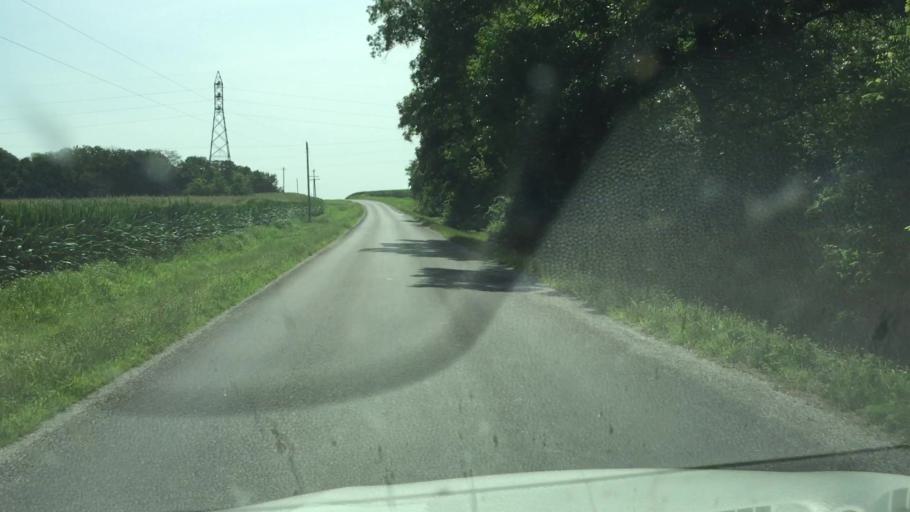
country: US
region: Illinois
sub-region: Hancock County
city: Nauvoo
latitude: 40.5119
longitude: -91.3538
